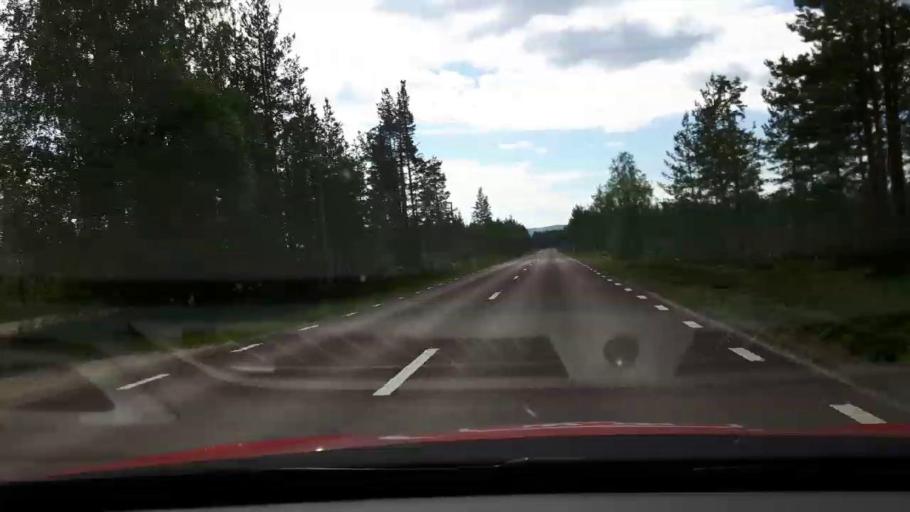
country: SE
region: Jaemtland
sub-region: Harjedalens Kommun
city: Sveg
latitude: 62.1239
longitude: 14.9710
